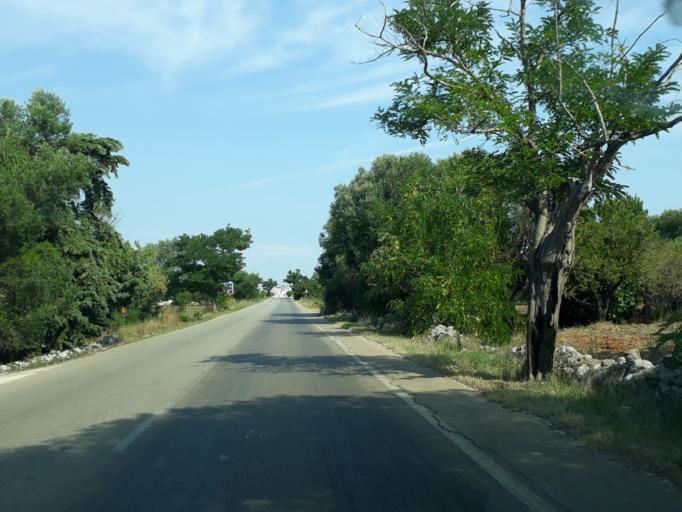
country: IT
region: Apulia
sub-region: Provincia di Brindisi
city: Carovigno
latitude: 40.6890
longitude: 17.6755
